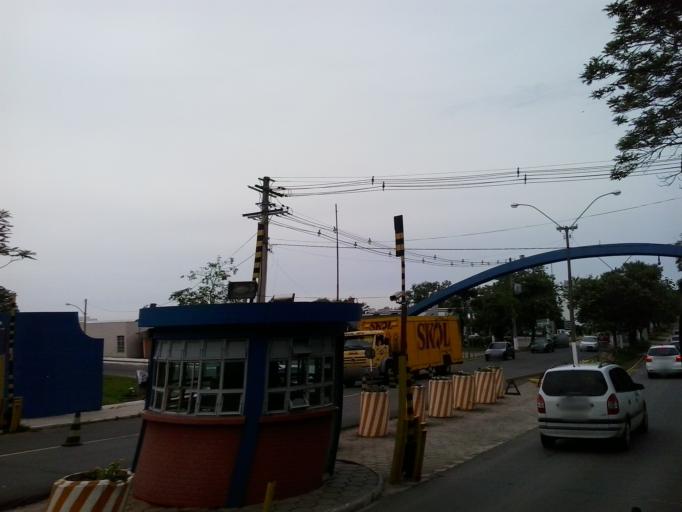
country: BR
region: Rio Grande do Sul
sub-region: Santa Maria
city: Santa Maria
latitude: -29.7103
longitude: -53.7167
